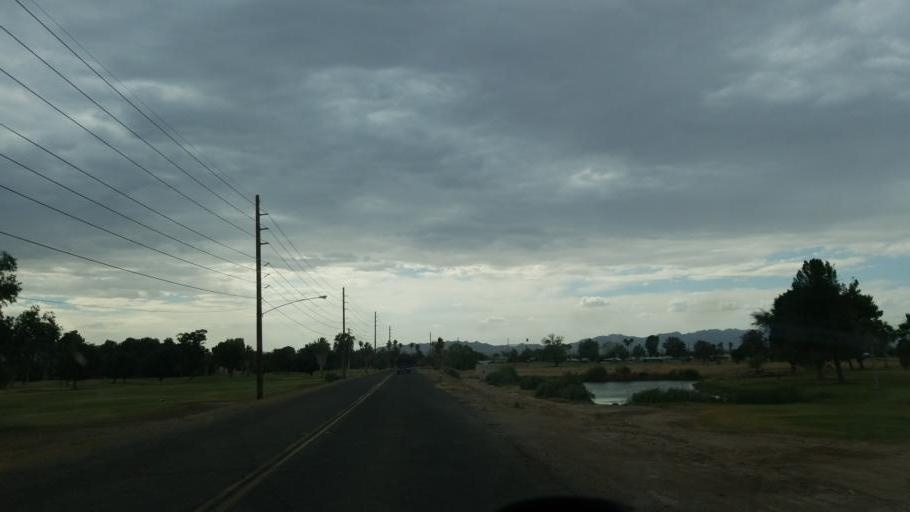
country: US
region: California
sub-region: San Bernardino County
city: Needles
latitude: 34.8437
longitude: -114.6021
